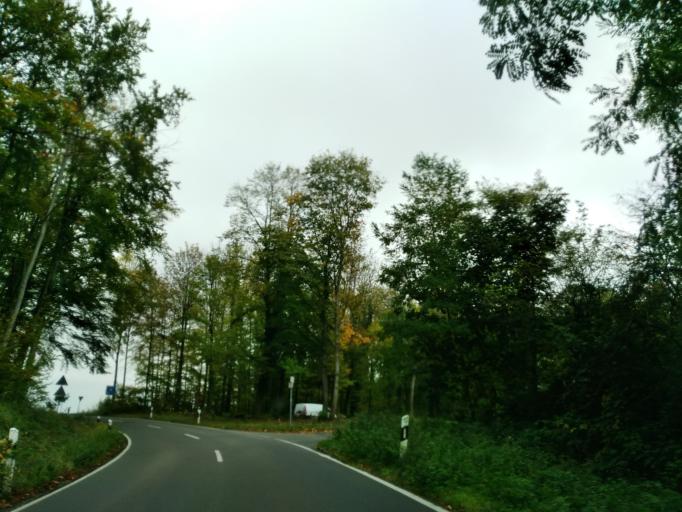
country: DE
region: North Rhine-Westphalia
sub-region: Regierungsbezirk Koln
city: Konigswinter
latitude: 50.7116
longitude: 7.1999
